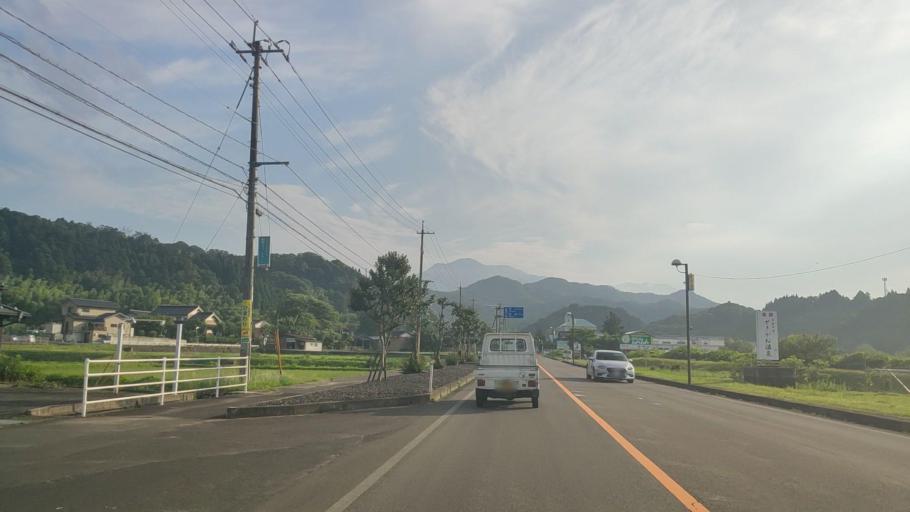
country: JP
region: Tottori
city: Kurayoshi
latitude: 35.3644
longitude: 133.7567
